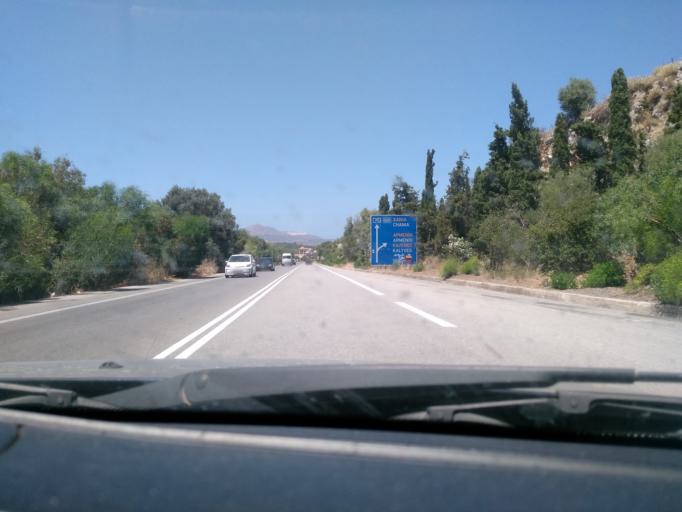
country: GR
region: Crete
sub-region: Nomos Chanias
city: Kalivai
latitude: 35.4343
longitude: 24.1660
